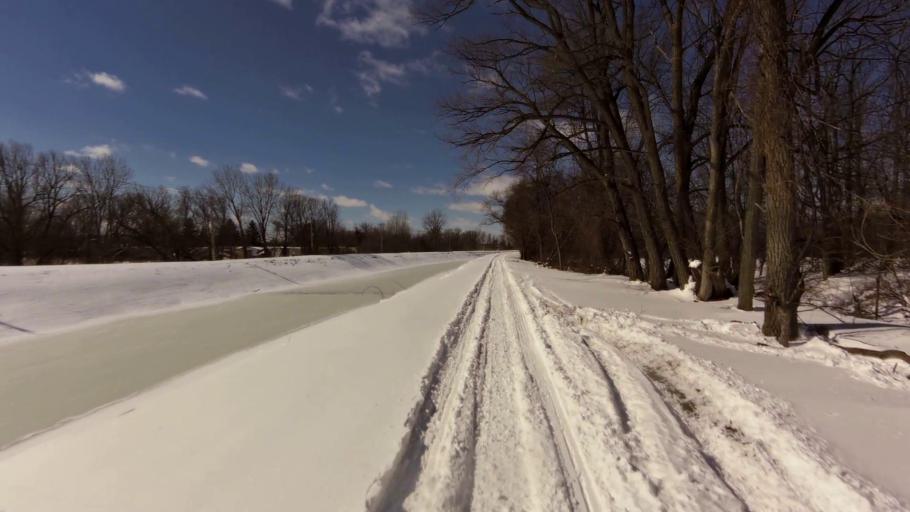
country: US
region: New York
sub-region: Orleans County
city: Albion
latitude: 43.2481
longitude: -78.2043
